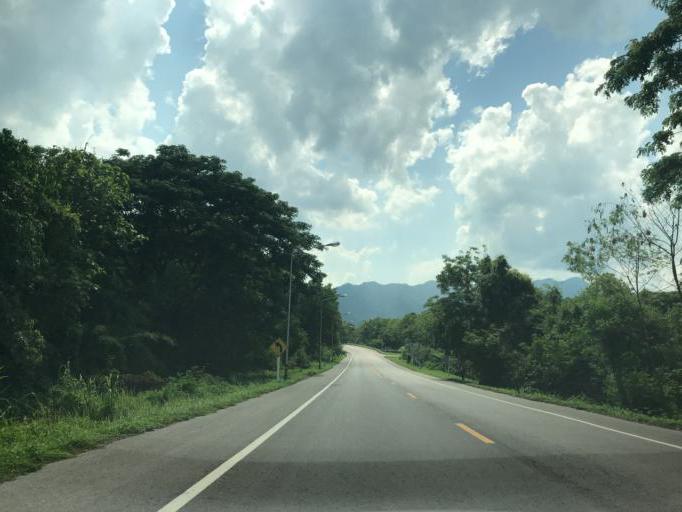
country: TH
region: Phayao
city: Phayao
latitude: 19.0919
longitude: 99.8304
